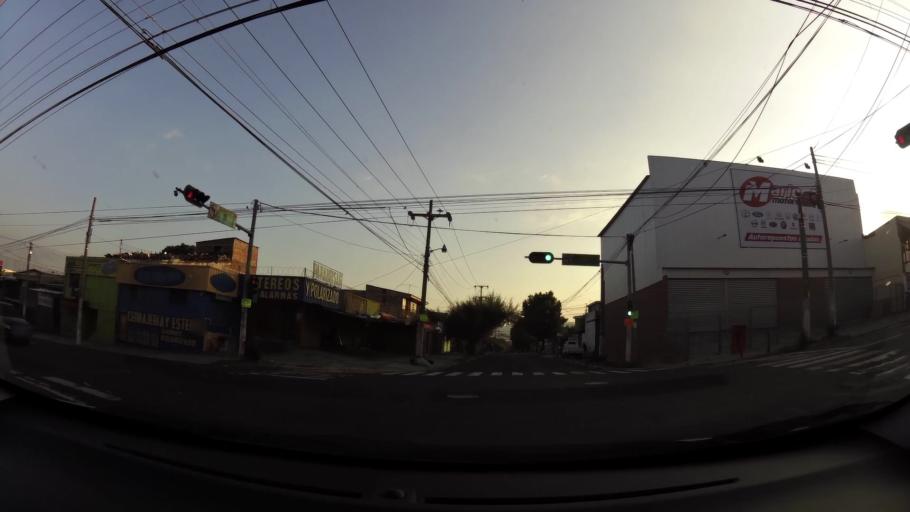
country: SV
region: San Salvador
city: San Salvador
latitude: 13.7142
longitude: -89.2007
